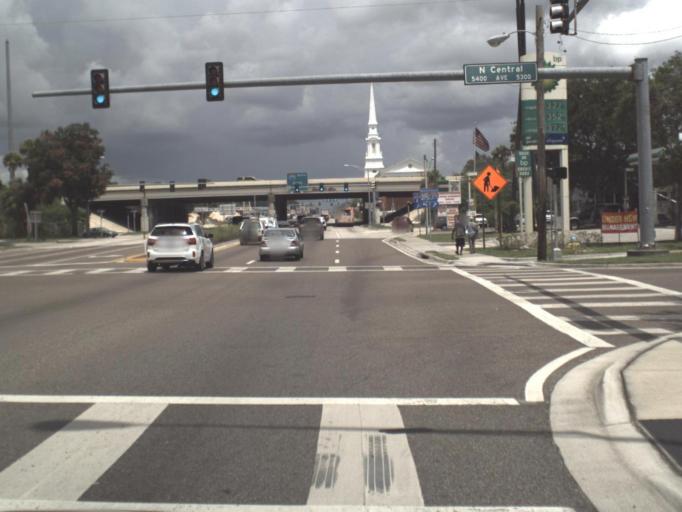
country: US
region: Florida
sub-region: Hillsborough County
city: Tampa
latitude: 27.9961
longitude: -82.4555
